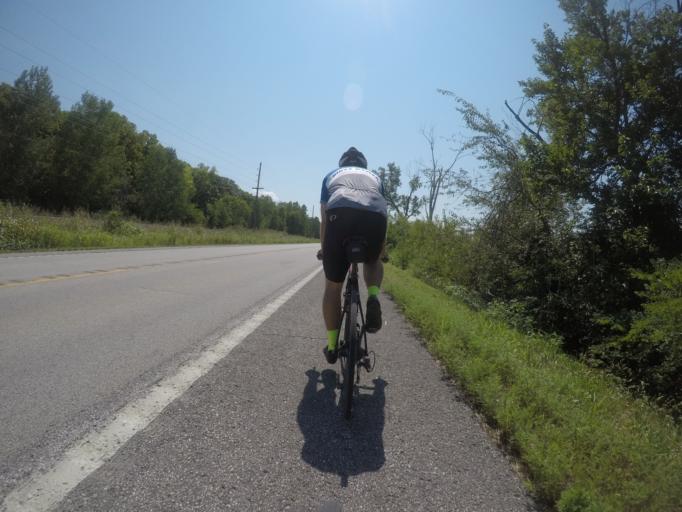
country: US
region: Missouri
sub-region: Platte County
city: Weston
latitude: 39.4871
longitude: -94.9954
